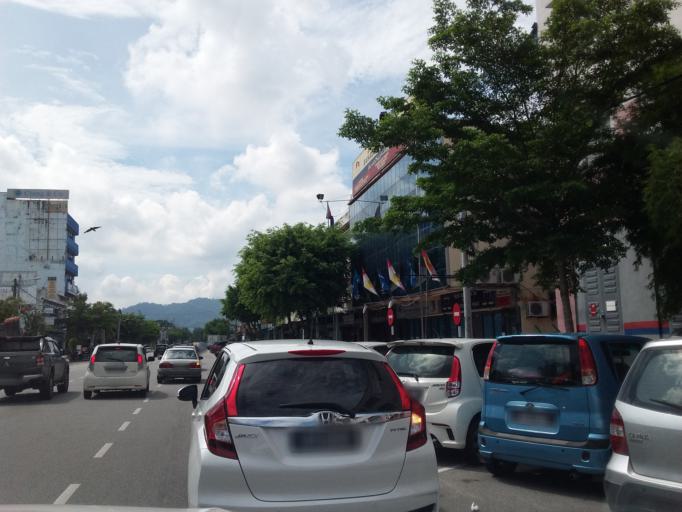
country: MY
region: Johor
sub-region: Daerah Batu Pahat
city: Batu Pahat
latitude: 1.8505
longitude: 102.9307
